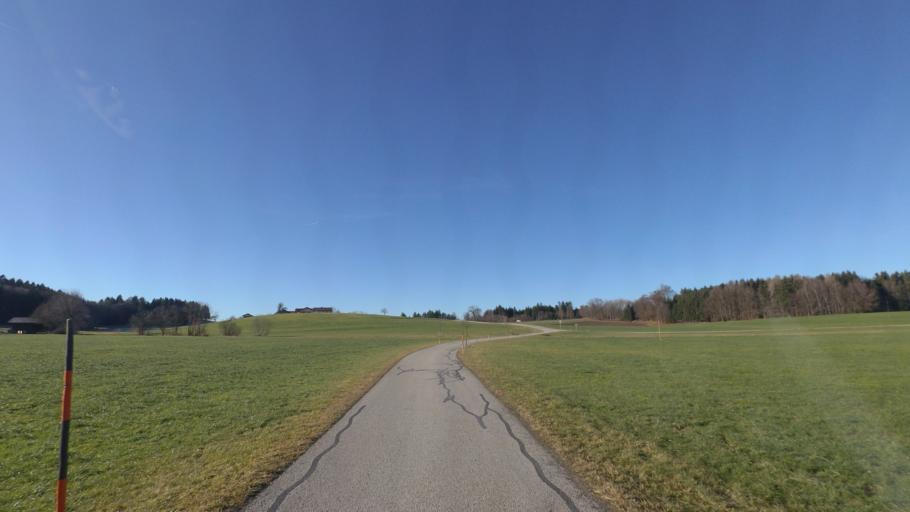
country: DE
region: Bavaria
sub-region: Upper Bavaria
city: Bergen
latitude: 47.8376
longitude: 12.5763
